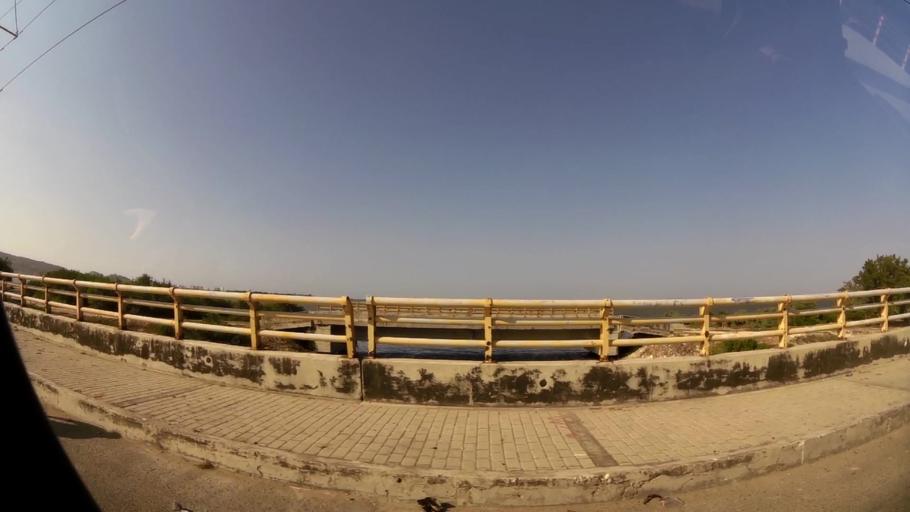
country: CO
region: Bolivar
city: Cartagena
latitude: 10.4148
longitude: -75.4978
